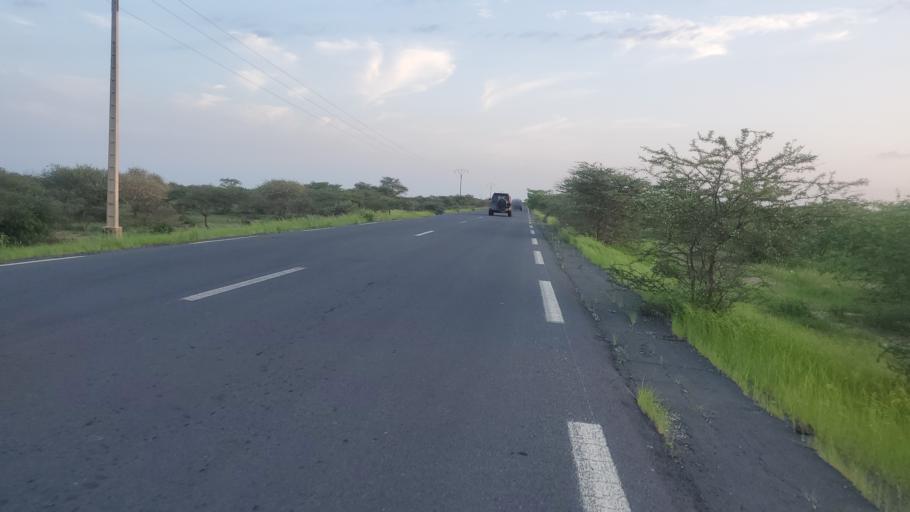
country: SN
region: Saint-Louis
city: Saint-Louis
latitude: 16.1262
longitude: -16.4134
